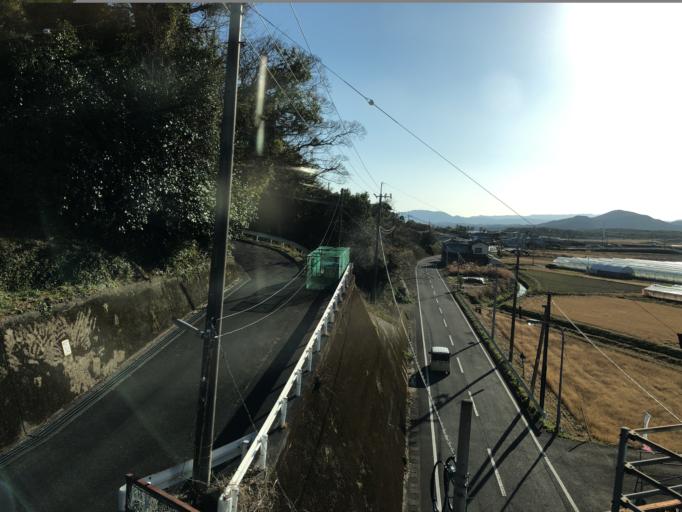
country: JP
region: Kochi
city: Nakamura
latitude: 33.0395
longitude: 133.0311
